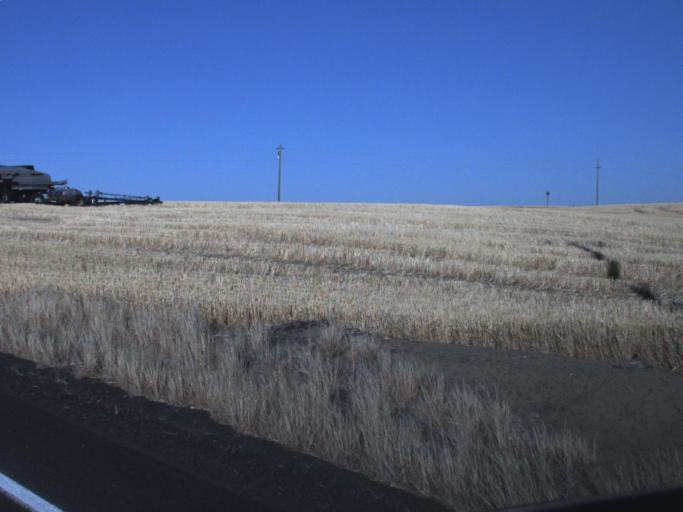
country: US
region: Washington
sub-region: Adams County
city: Ritzville
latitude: 46.9270
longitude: -118.3434
